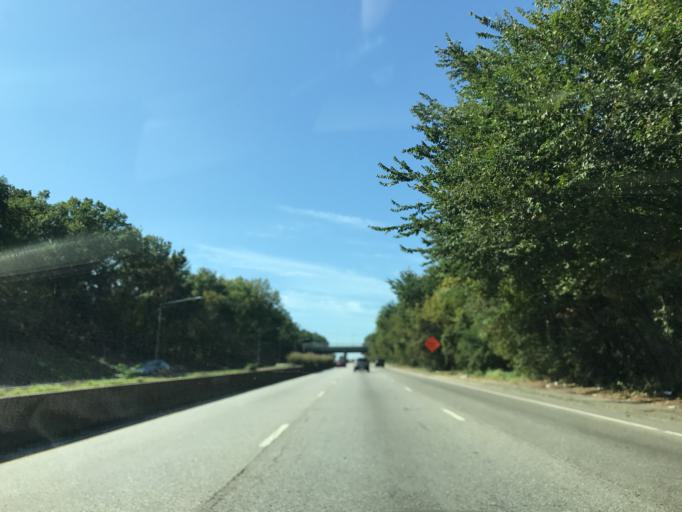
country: US
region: Maryland
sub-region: Baltimore County
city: Baltimore Highlands
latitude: 39.2526
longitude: -76.6395
